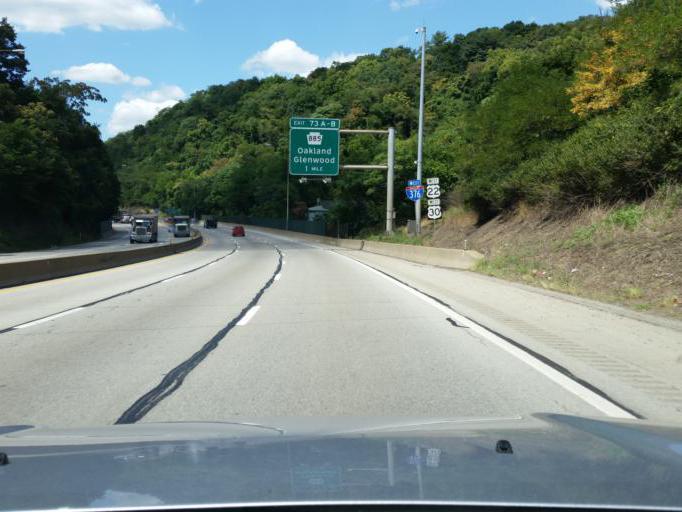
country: US
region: Pennsylvania
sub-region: Allegheny County
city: Bloomfield
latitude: 40.4292
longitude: -79.9407
